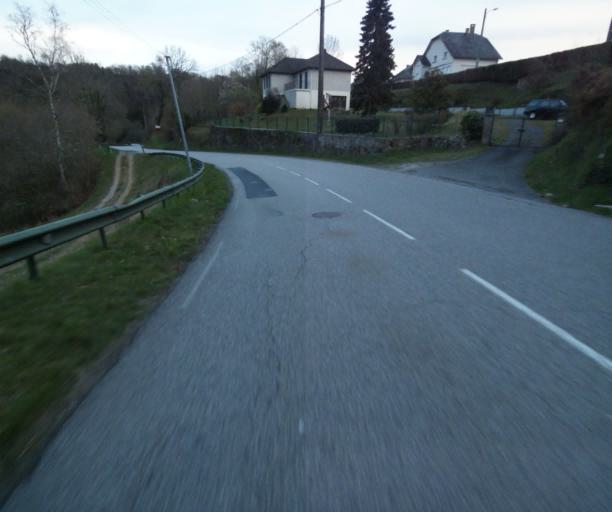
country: FR
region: Limousin
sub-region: Departement de la Correze
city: Correze
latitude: 45.3668
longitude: 1.8728
